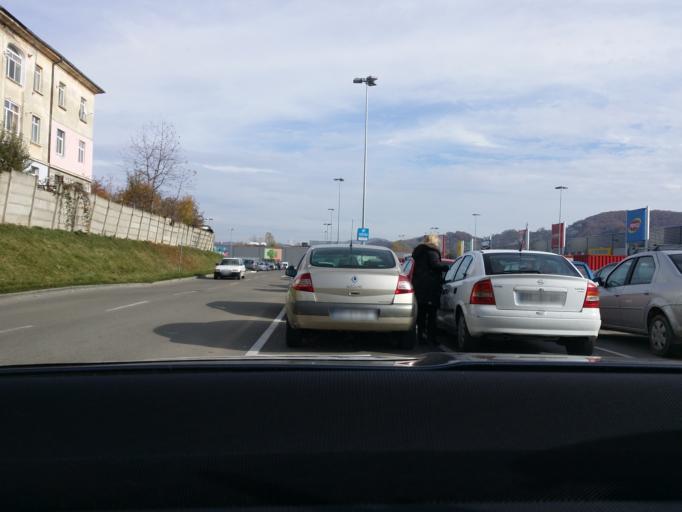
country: RO
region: Prahova
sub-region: Municipiul Campina
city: Campina
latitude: 45.1158
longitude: 25.7447
